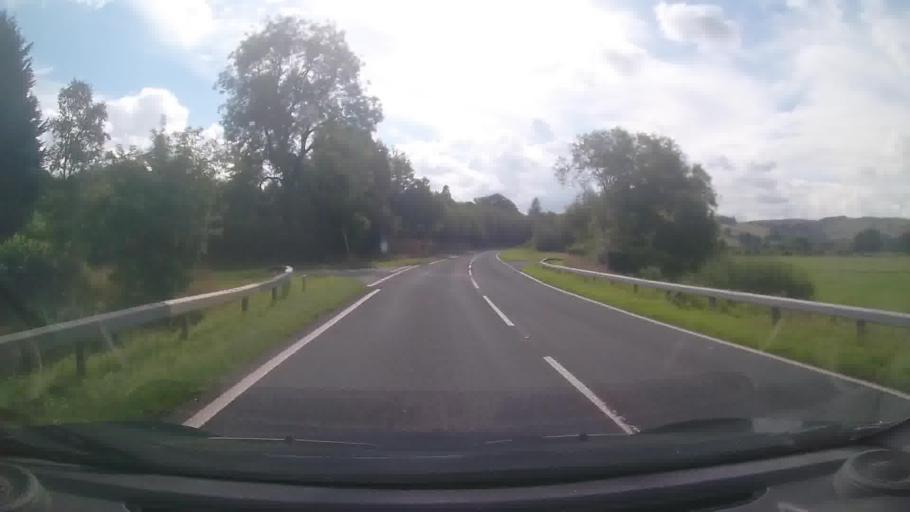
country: GB
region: Wales
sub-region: Sir Powys
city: Mochdre
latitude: 52.3825
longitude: -3.3272
